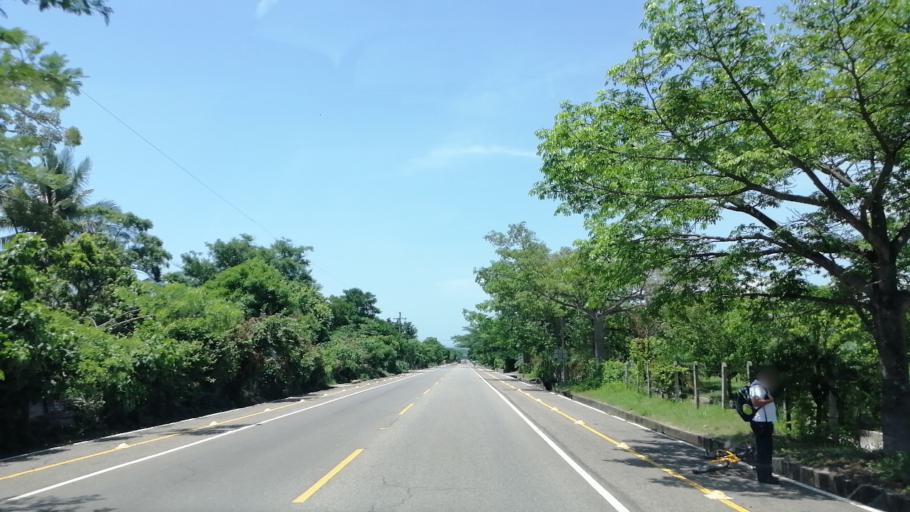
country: SV
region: Chalatenango
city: Nueva Concepcion
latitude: 14.1409
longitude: -89.2968
